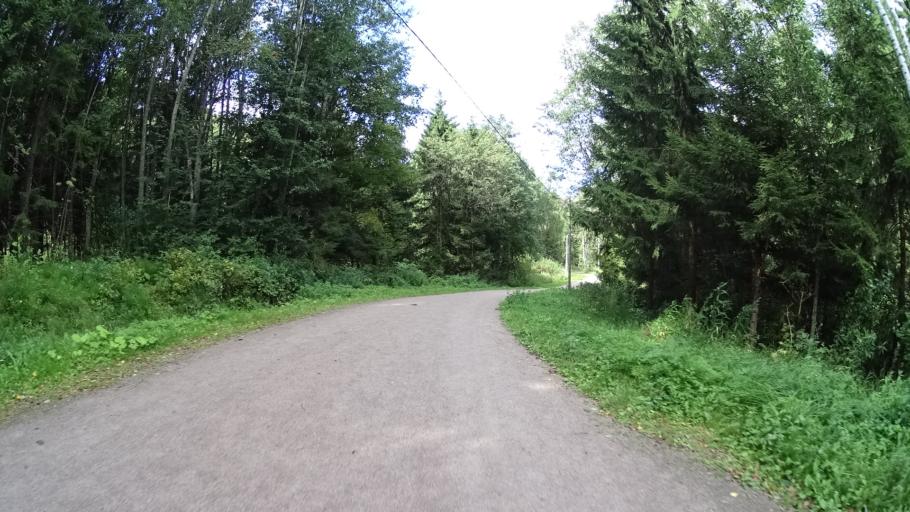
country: FI
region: Uusimaa
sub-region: Helsinki
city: Kilo
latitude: 60.2338
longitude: 24.7957
